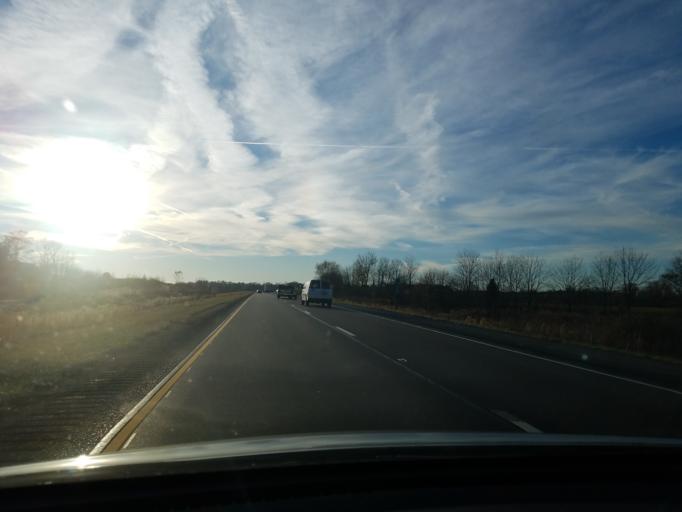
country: US
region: Indiana
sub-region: Dubois County
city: Ferdinand
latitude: 38.2043
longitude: -86.8191
